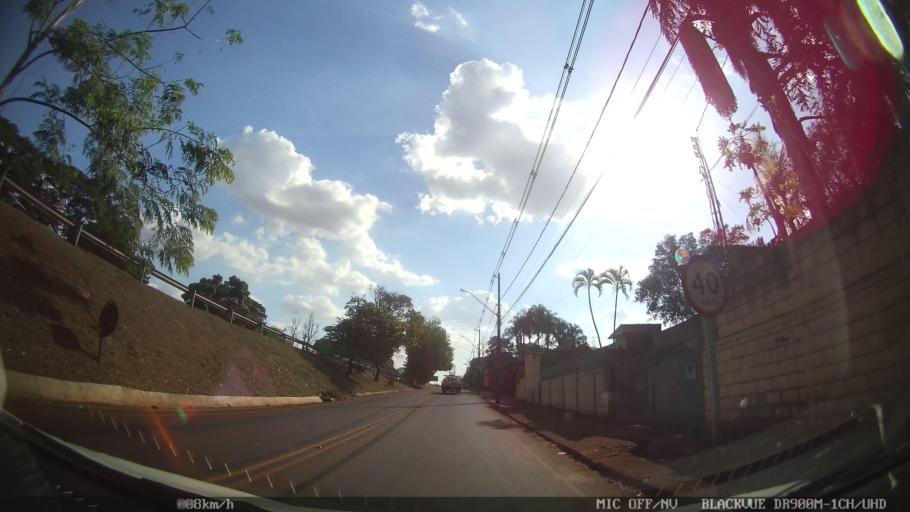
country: BR
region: Sao Paulo
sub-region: Ribeirao Preto
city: Ribeirao Preto
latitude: -21.1780
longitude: -47.8412
